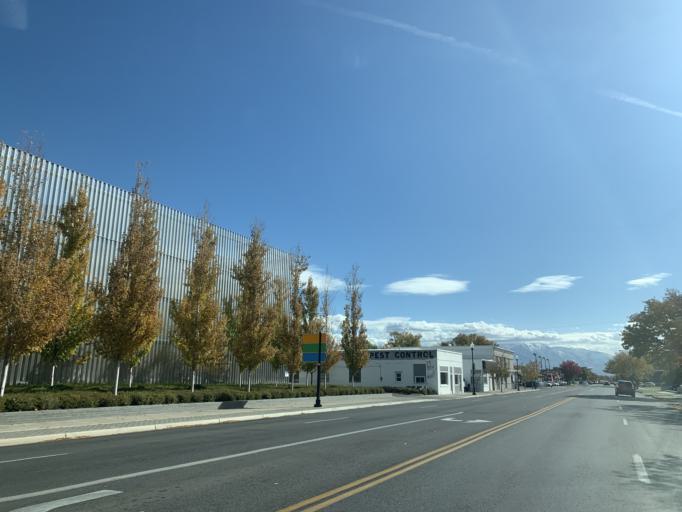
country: US
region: Utah
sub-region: Utah County
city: Provo
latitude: 40.2322
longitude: -111.6623
